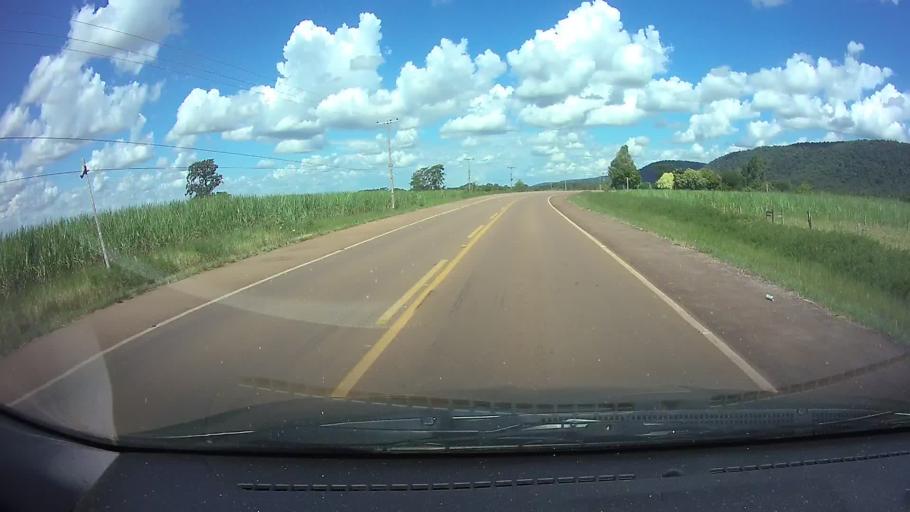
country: PY
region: Paraguari
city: La Colmena
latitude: -25.9068
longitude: -56.7627
